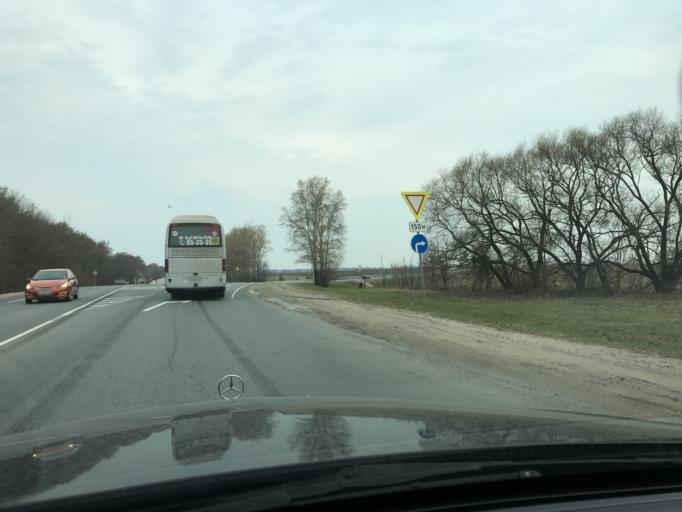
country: RU
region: Vladimir
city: Suzdal'
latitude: 56.3834
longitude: 40.4553
